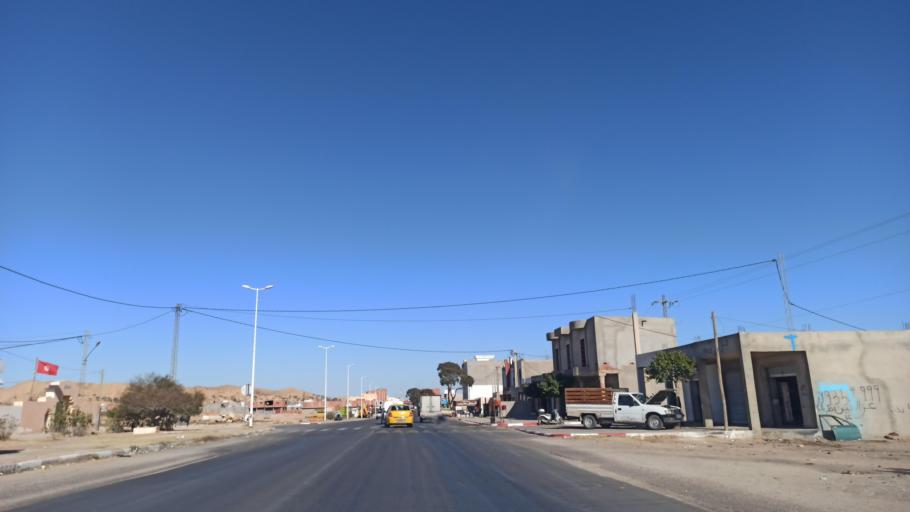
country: TN
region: Sidi Bu Zayd
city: Bi'r al Hufayy
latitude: 34.9164
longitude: 9.1850
